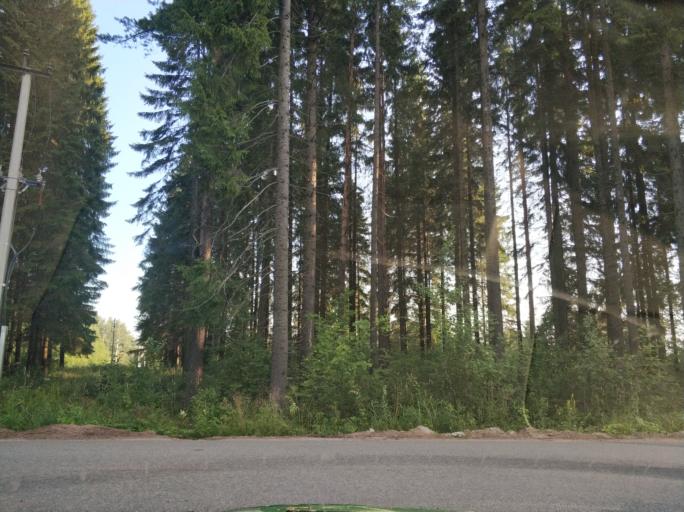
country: RU
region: Leningrad
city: Shcheglovo
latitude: 60.0565
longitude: 30.7486
